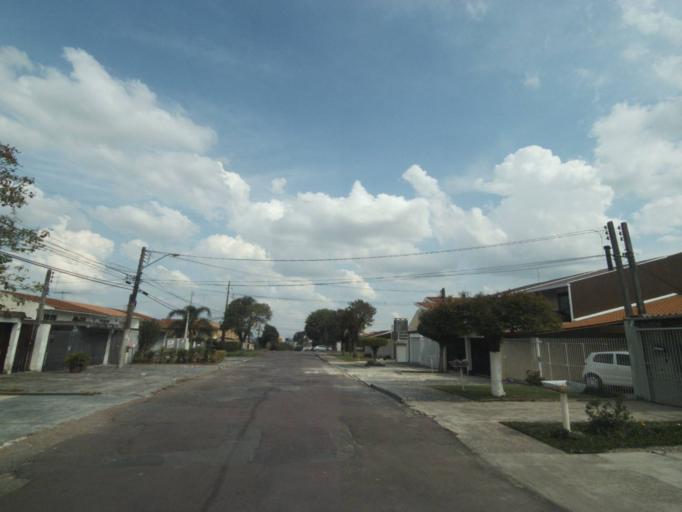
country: BR
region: Parana
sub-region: Pinhais
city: Pinhais
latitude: -25.4111
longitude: -49.2083
